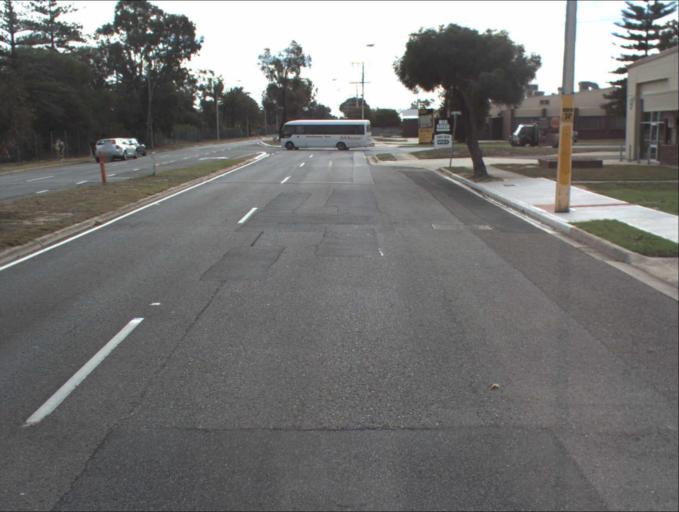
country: AU
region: South Australia
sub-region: Charles Sturt
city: Royal Park
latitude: -34.8663
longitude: 138.5029
